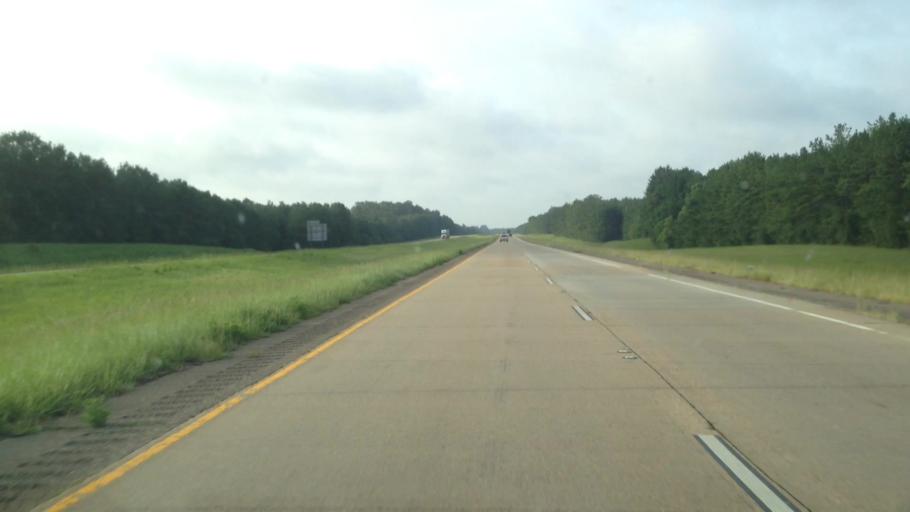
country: US
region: Louisiana
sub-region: Rapides Parish
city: Lecompte
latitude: 31.0568
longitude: -92.4254
